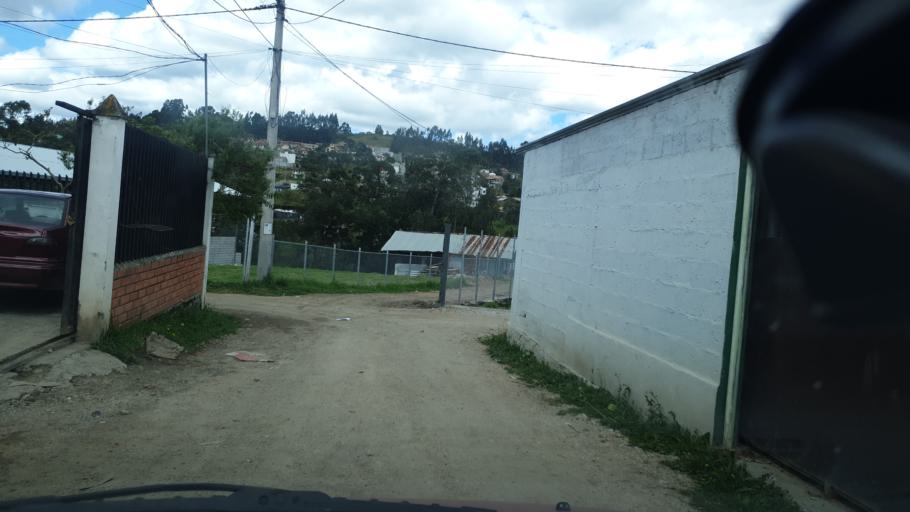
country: EC
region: Azuay
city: Cuenca
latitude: -2.9336
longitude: -78.9677
